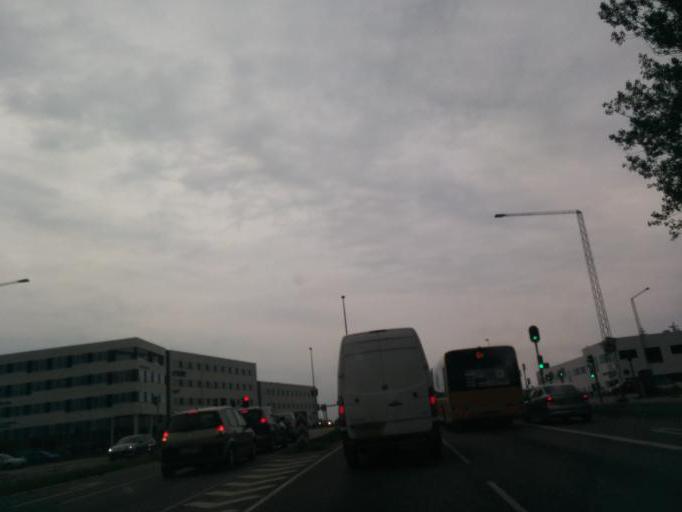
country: DK
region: Central Jutland
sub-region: Arhus Kommune
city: Stavtrup
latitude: 56.1701
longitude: 10.1551
